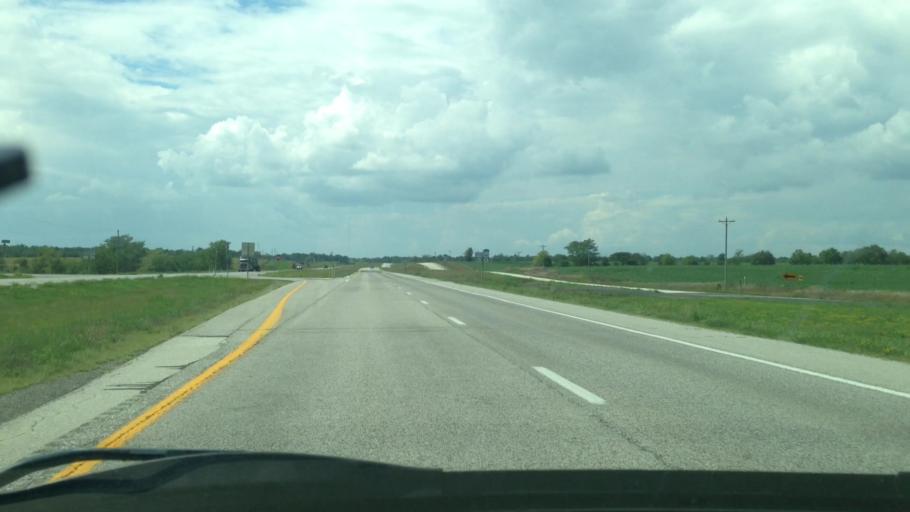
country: US
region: Missouri
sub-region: Pike County
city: Bowling Green
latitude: 39.2500
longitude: -91.0345
